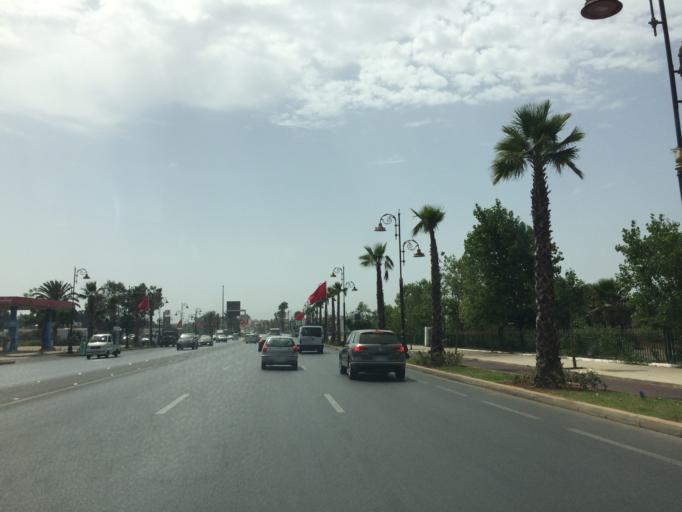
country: MA
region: Rabat-Sale-Zemmour-Zaer
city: Sale
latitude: 34.0344
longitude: -6.7849
